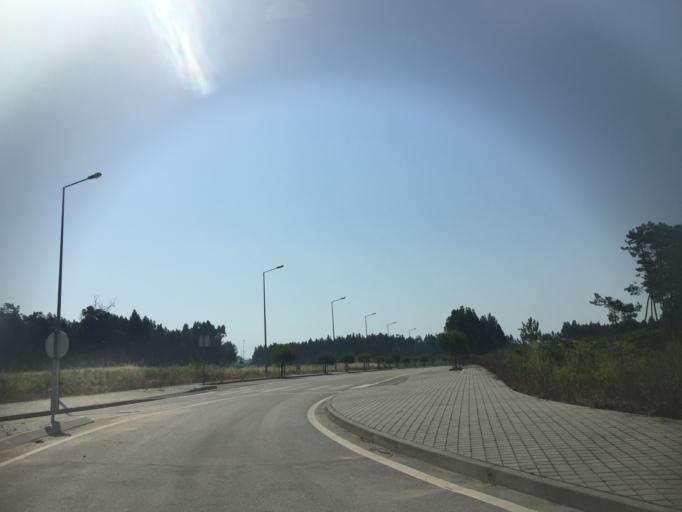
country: PT
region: Coimbra
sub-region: Cantanhede
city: Cantanhede
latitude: 40.4264
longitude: -8.5464
